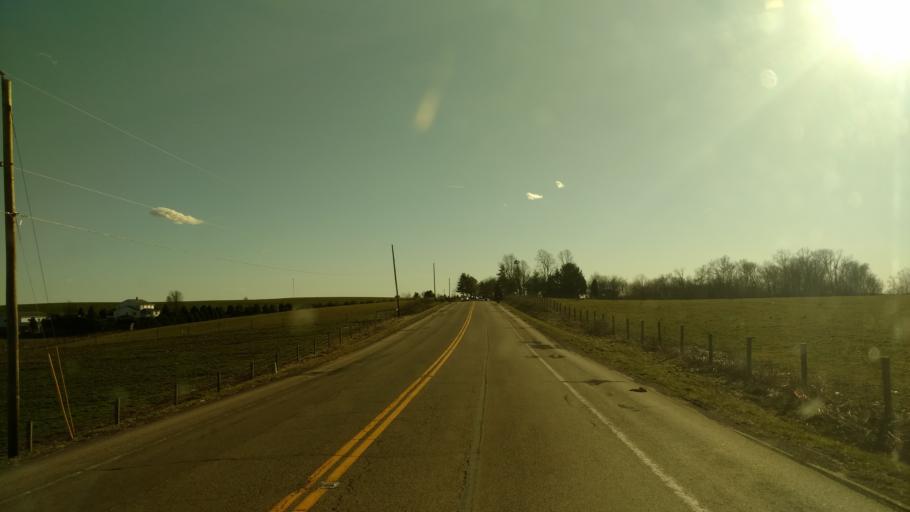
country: US
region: Ohio
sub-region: Holmes County
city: Millersburg
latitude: 40.5817
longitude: -81.7720
